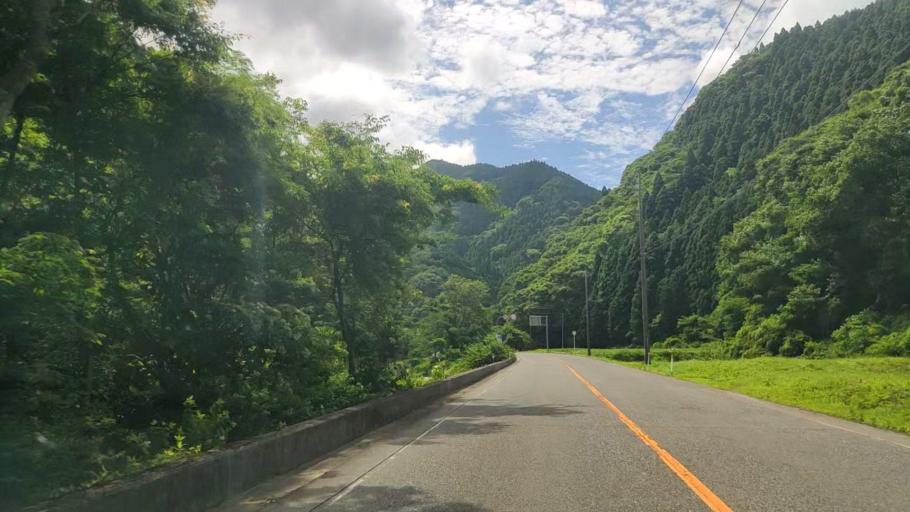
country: JP
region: Okayama
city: Niimi
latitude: 35.2124
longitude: 133.4657
